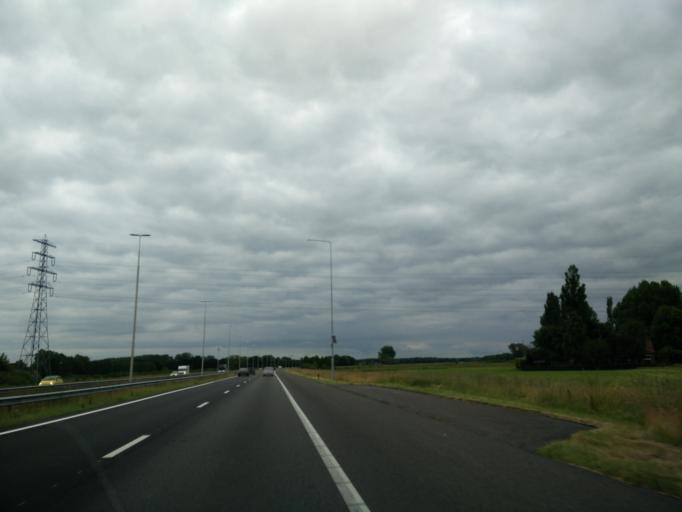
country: NL
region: Gelderland
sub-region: Gemeente Epe
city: Emst
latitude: 52.3131
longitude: 6.0069
